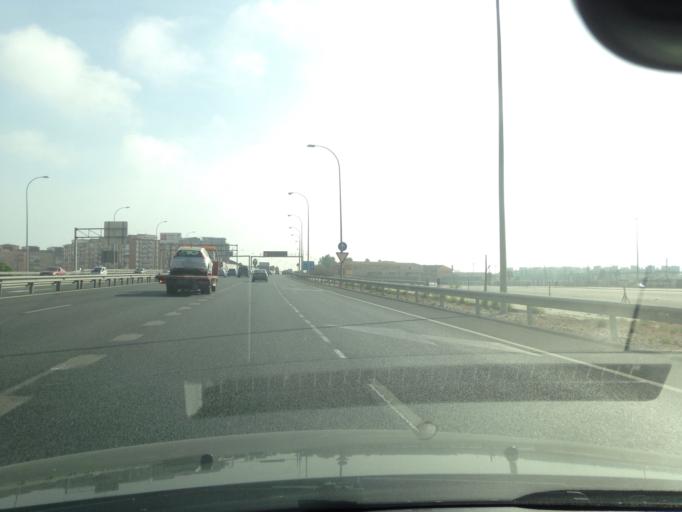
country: ES
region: Andalusia
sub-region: Provincia de Malaga
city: Malaga
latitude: 36.7023
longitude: -4.4580
